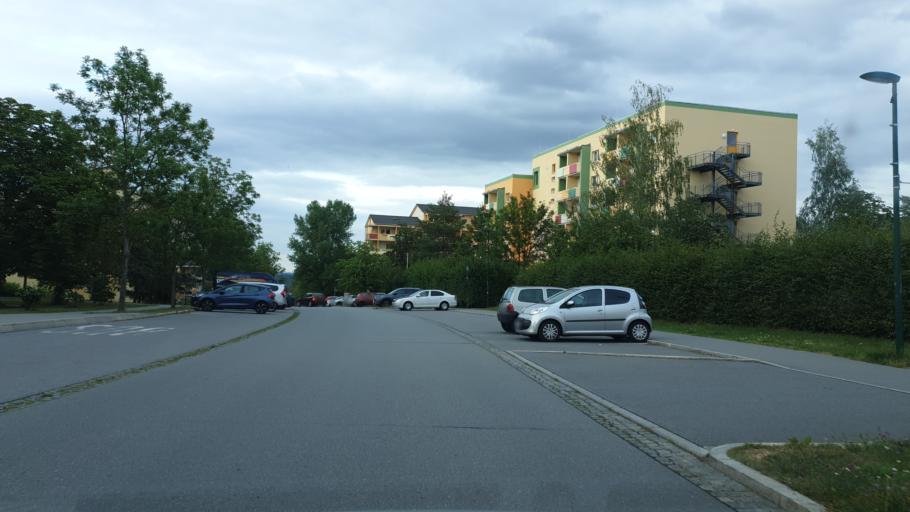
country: DE
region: Saxony
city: Stollberg
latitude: 50.7136
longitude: 12.7679
